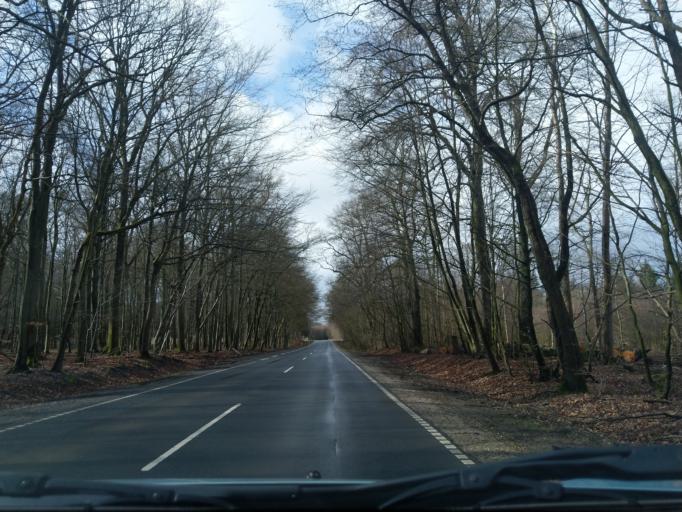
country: DK
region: Zealand
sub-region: Naestved Kommune
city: Fuglebjerg
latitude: 55.3260
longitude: 11.5946
